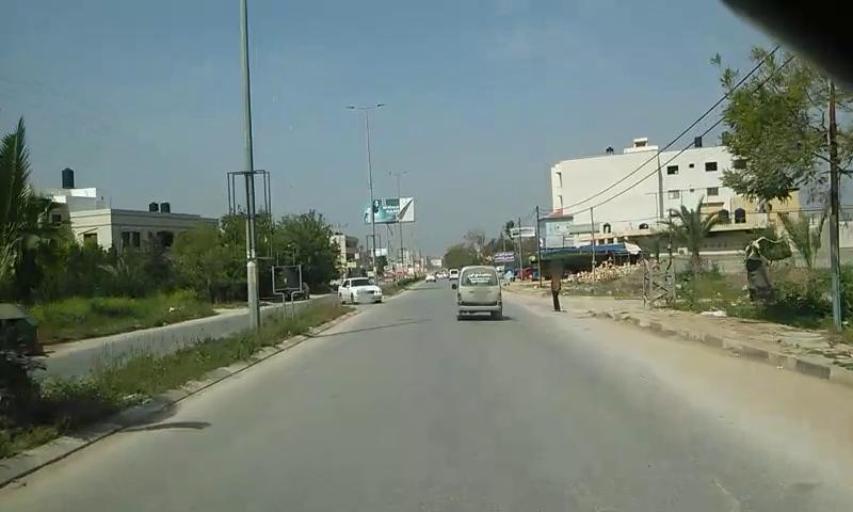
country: PS
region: West Bank
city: Janin
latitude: 32.4720
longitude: 35.3028
